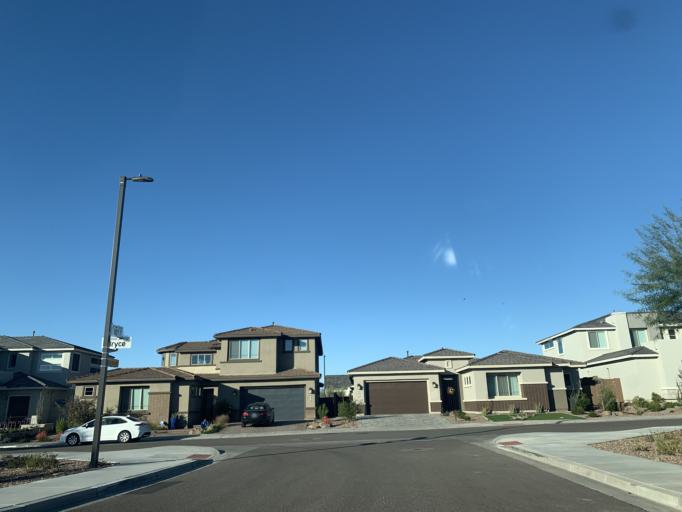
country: US
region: Arizona
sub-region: Maricopa County
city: Cave Creek
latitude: 33.6883
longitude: -112.0168
